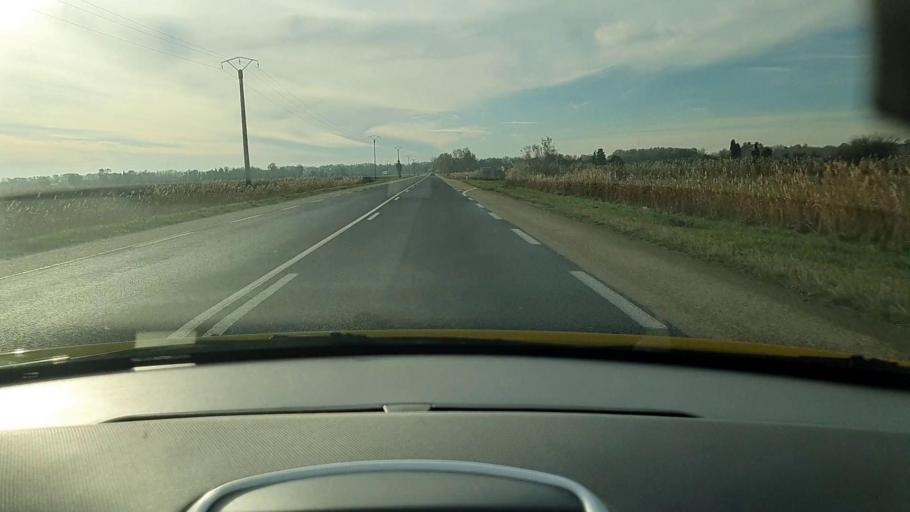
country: FR
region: Languedoc-Roussillon
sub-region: Departement du Gard
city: Bellegarde
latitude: 43.7166
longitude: 4.5485
